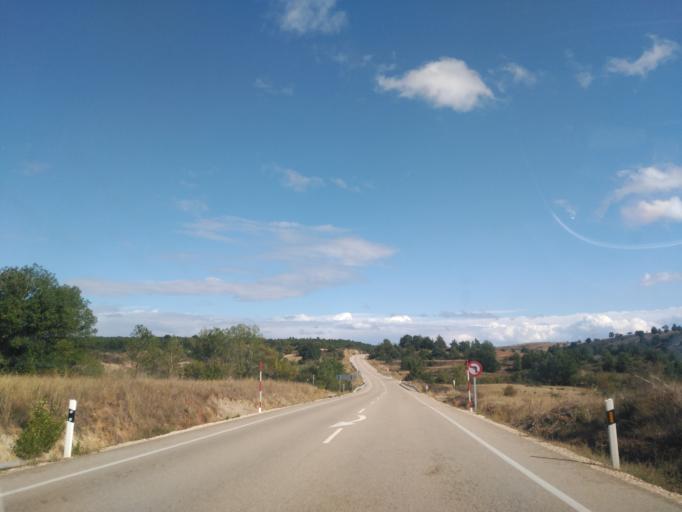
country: ES
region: Castille and Leon
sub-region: Provincia de Burgos
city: Cabezon de la Sierra
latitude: 41.8963
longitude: -3.2635
